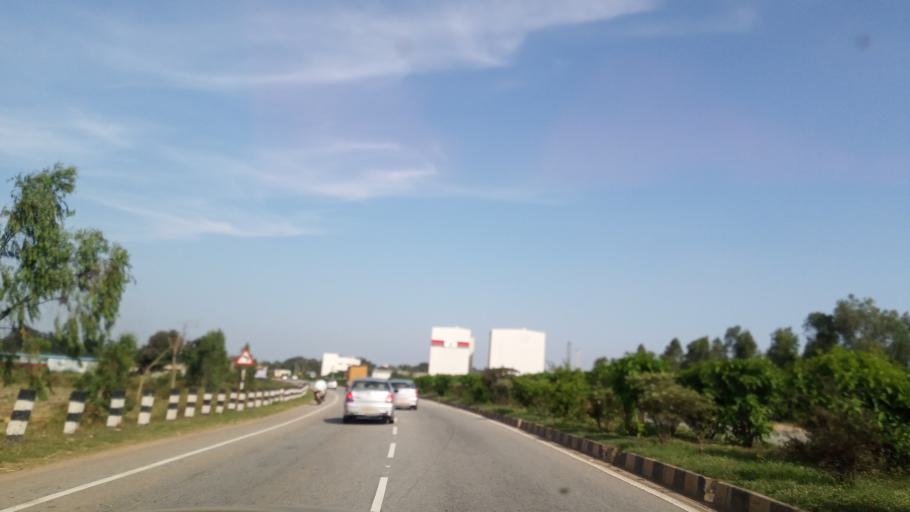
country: IN
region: Karnataka
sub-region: Bangalore Rural
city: Dasarahalli
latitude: 13.1202
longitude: 77.8959
